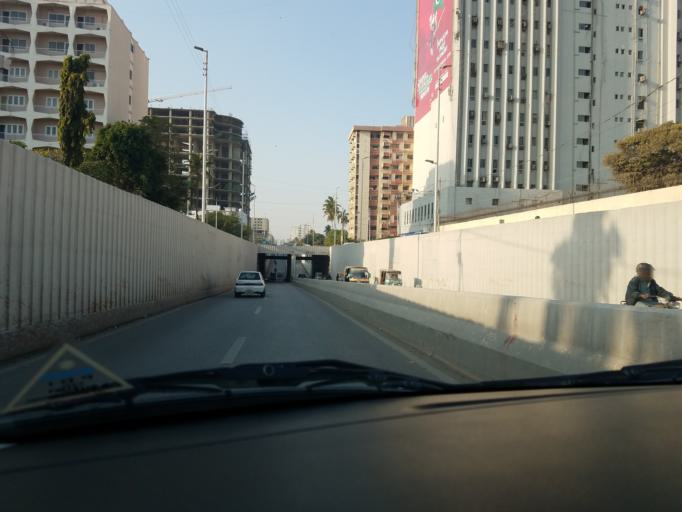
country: PK
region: Sindh
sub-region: Karachi District
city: Karachi
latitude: 24.8514
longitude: 67.0347
